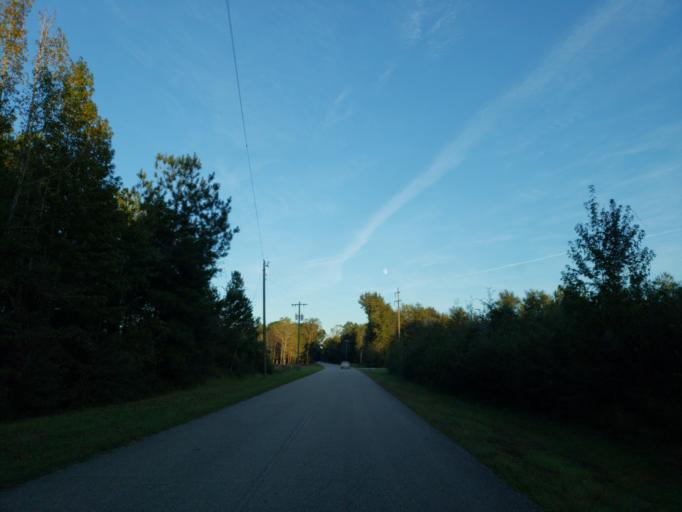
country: US
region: Mississippi
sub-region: Wayne County
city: Belmont
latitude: 31.4361
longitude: -88.4872
